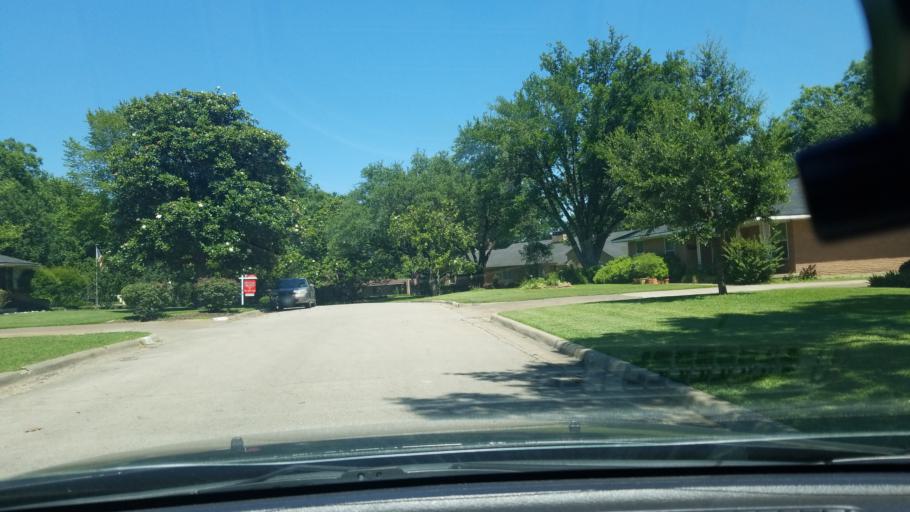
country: US
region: Texas
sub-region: Dallas County
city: Mesquite
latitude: 32.7539
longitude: -96.6038
